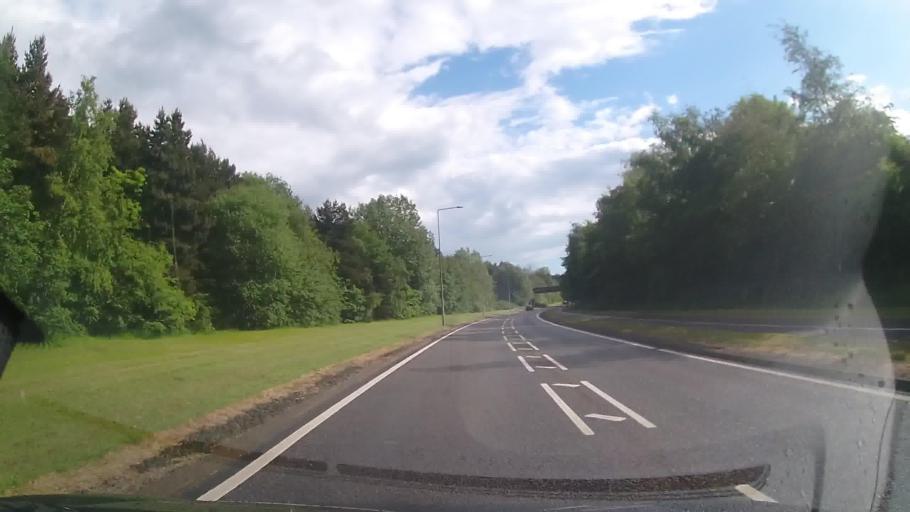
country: GB
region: England
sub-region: Telford and Wrekin
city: Telford
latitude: 52.6838
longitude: -2.4630
